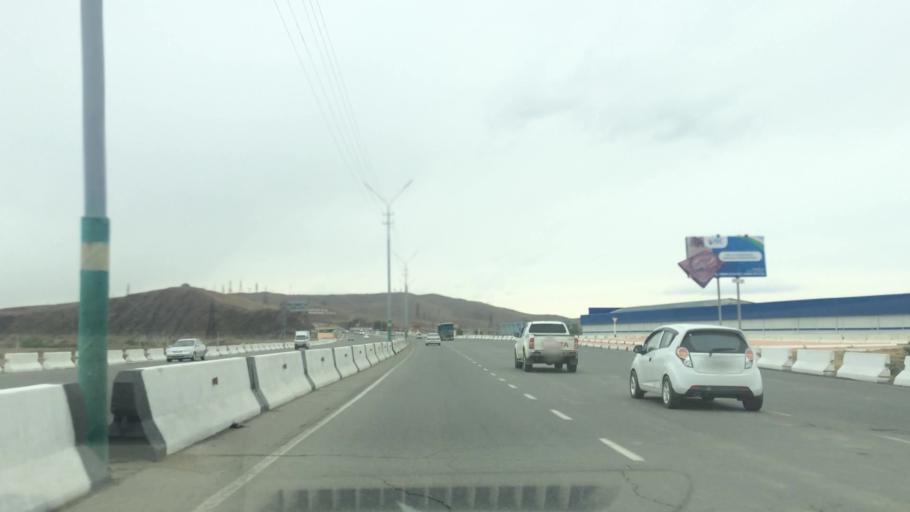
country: UZ
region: Samarqand
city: Jomboy
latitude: 39.6908
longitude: 67.0641
